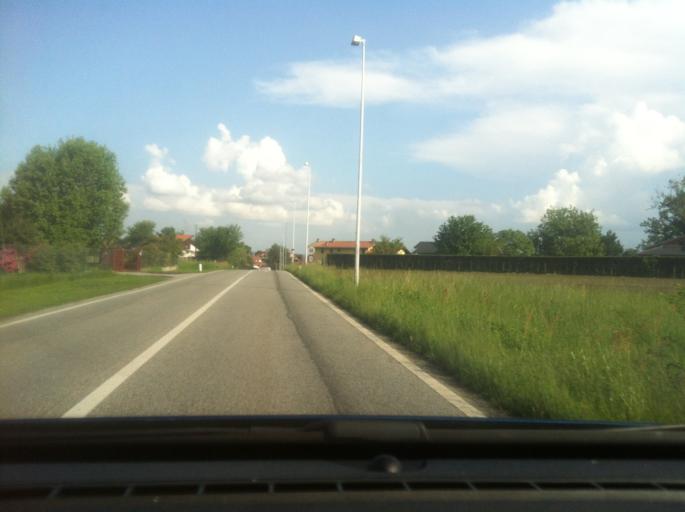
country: IT
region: Piedmont
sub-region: Provincia di Torino
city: Pavone Canavese
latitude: 45.4327
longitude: 7.8530
